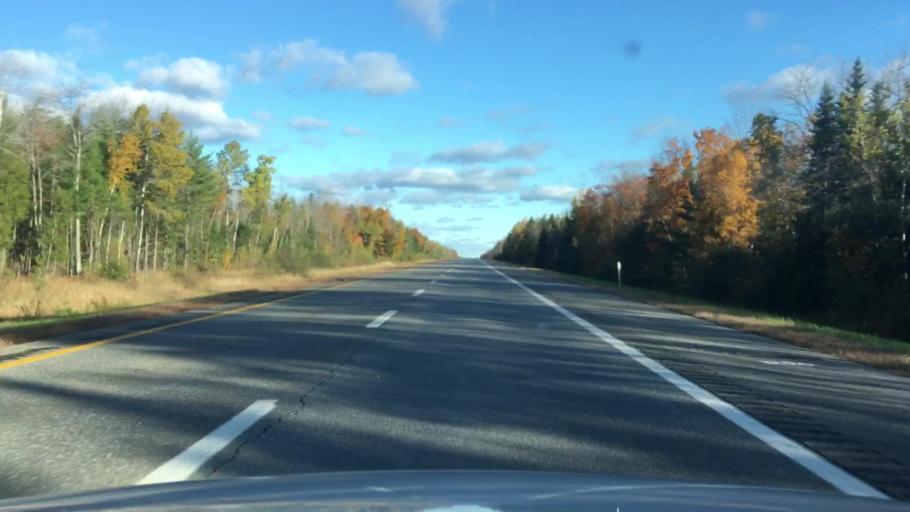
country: US
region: Maine
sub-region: Penobscot County
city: Greenbush
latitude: 45.0744
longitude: -68.6910
